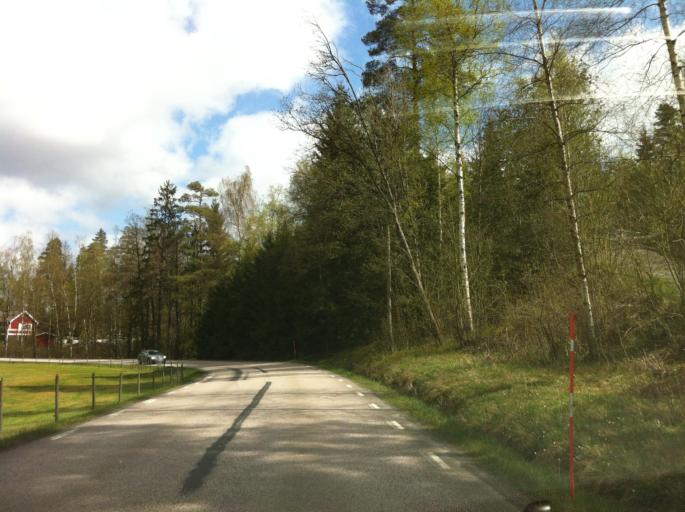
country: SE
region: Vaestra Goetaland
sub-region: Alingsas Kommun
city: Alingsas
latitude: 57.8495
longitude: 12.5584
